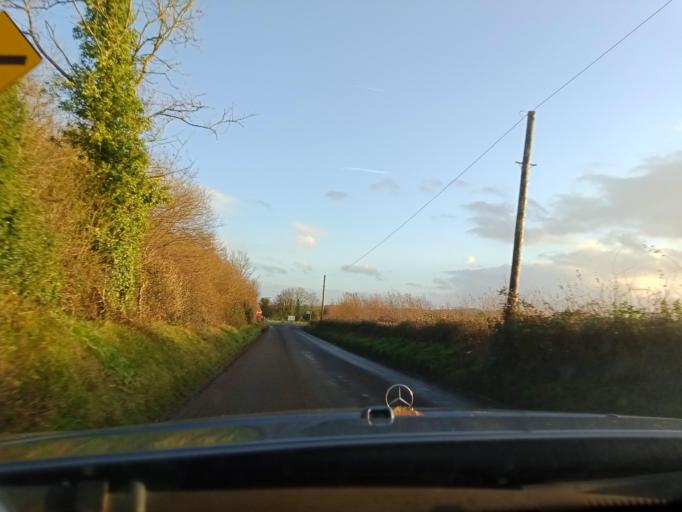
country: IE
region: Leinster
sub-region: Kilkenny
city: Callan
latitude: 52.4905
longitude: -7.3239
